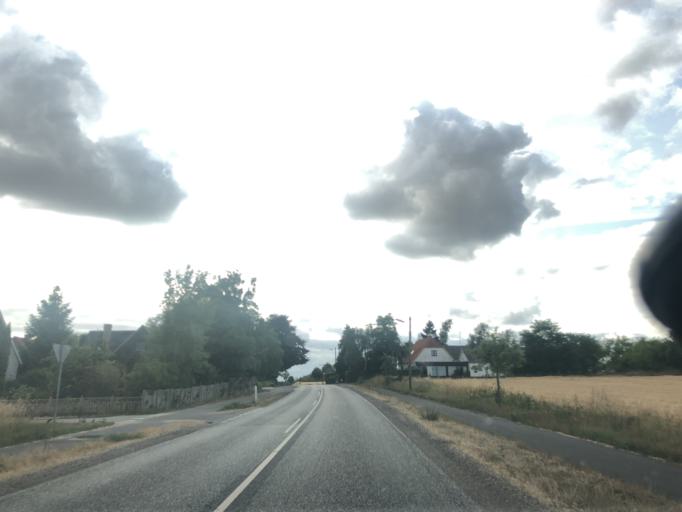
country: DK
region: Zealand
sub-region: Koge Kommune
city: Bjaeverskov
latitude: 55.4216
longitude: 12.0087
